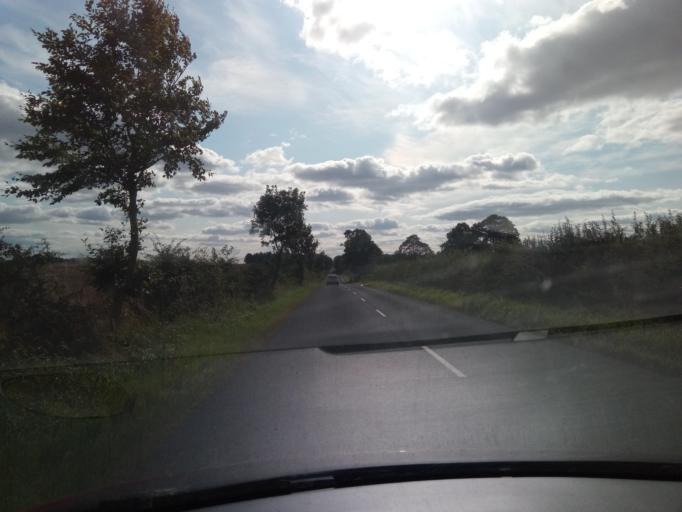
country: GB
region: Scotland
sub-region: The Scottish Borders
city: Allanton
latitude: 55.7312
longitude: -2.2291
